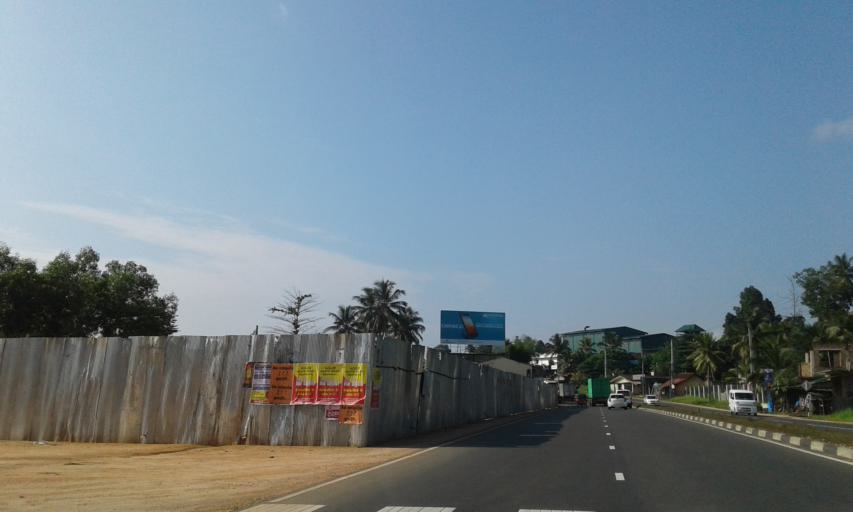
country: LK
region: Western
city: Gampaha
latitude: 7.0587
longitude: 80.0088
